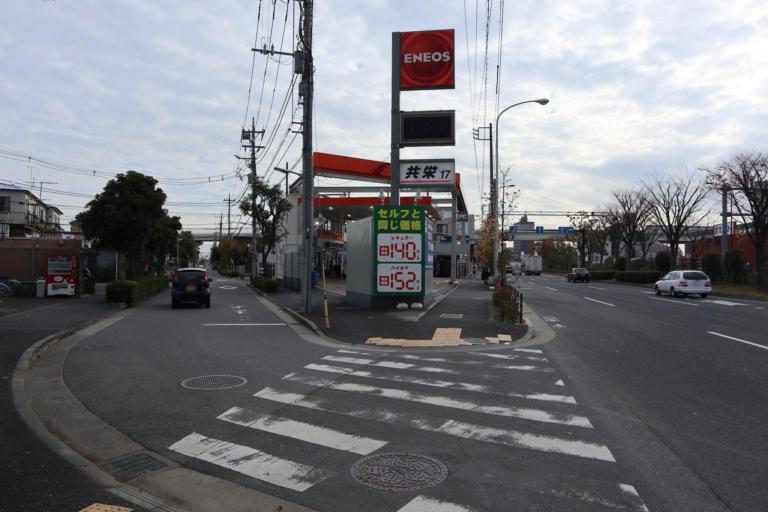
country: JP
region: Tokyo
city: Urayasu
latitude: 35.6995
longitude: 139.8820
